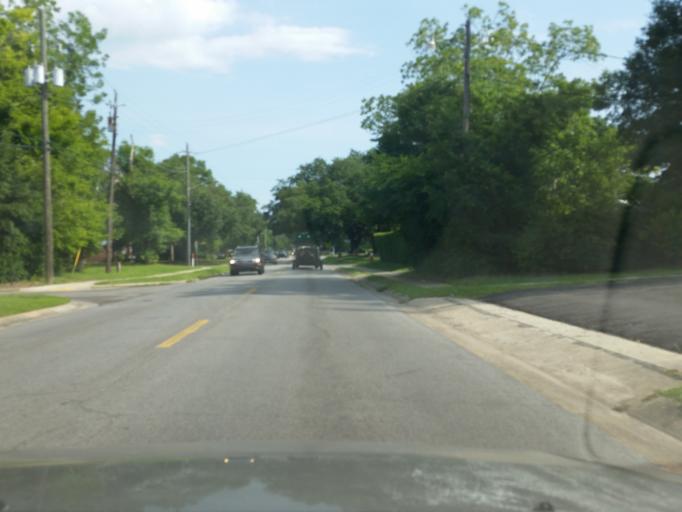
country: US
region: Florida
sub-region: Escambia County
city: Goulding
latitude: 30.4480
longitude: -87.2081
